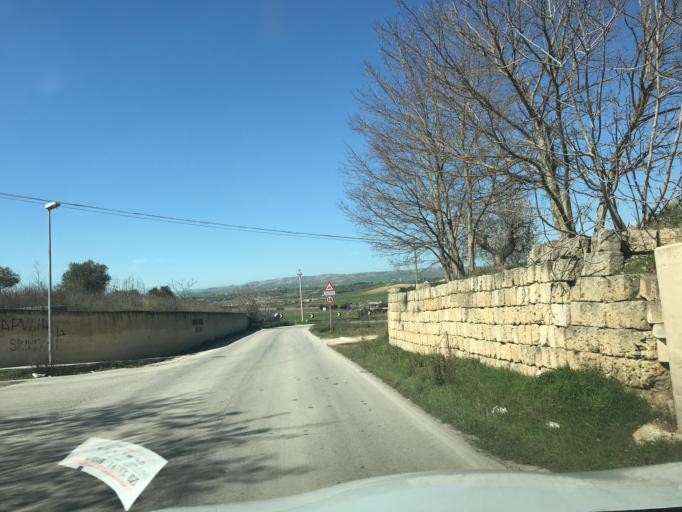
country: IT
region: Apulia
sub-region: Provincia di Bari
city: Gravina in Puglia
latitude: 40.8355
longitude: 16.4262
